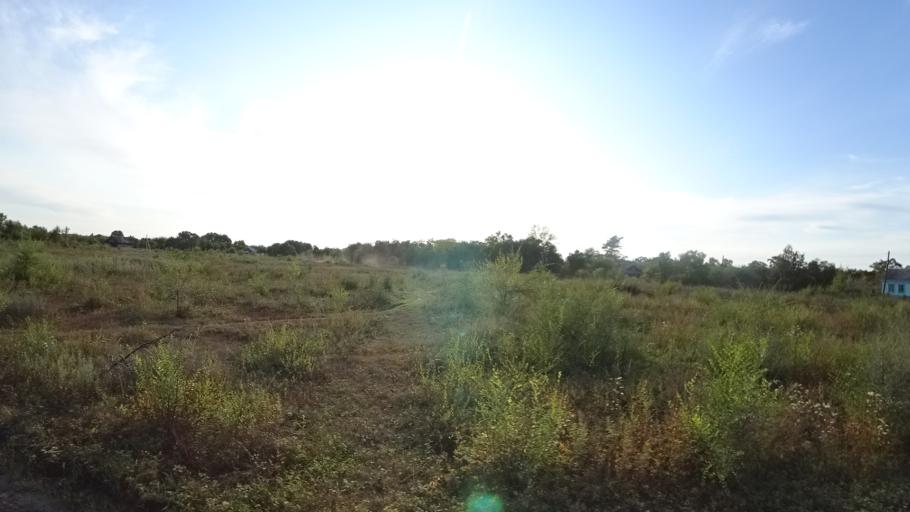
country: RU
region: Amur
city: Arkhara
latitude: 49.3539
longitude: 130.1100
